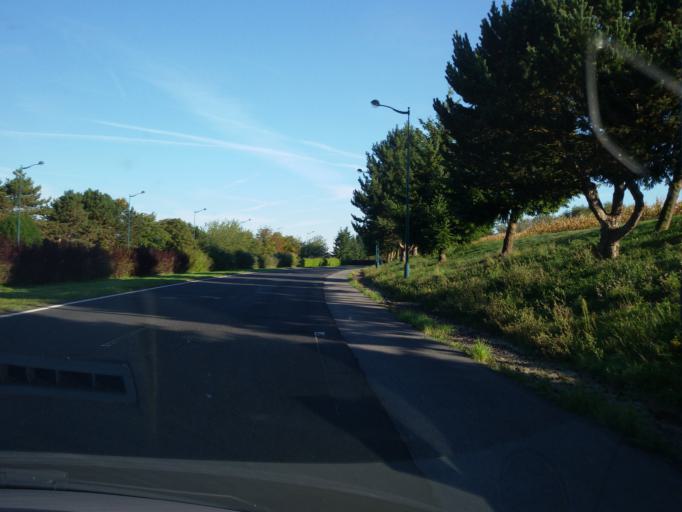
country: FR
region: Ile-de-France
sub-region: Departement de Seine-et-Marne
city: Serris
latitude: 48.8600
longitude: 2.7946
